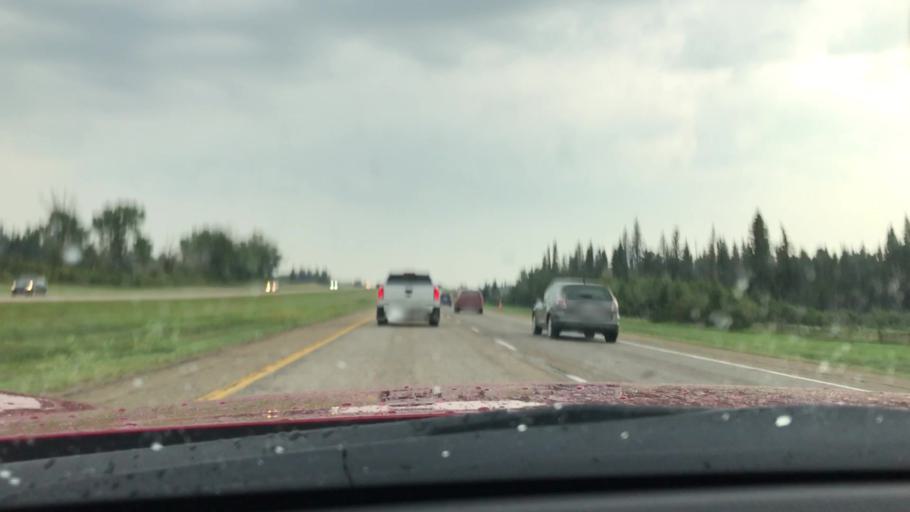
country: CA
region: Alberta
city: Ponoka
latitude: 52.6194
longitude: -113.6637
